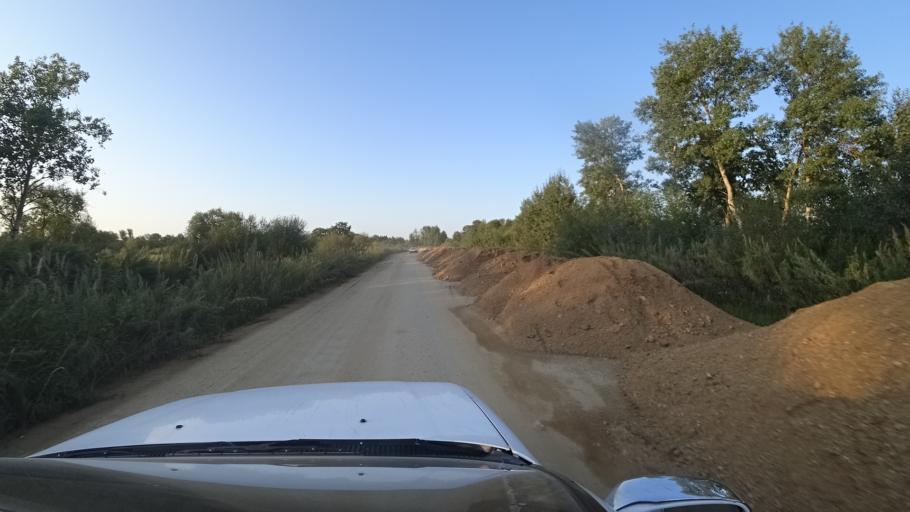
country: RU
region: Primorskiy
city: Dal'nerechensk
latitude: 45.9396
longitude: 133.7605
